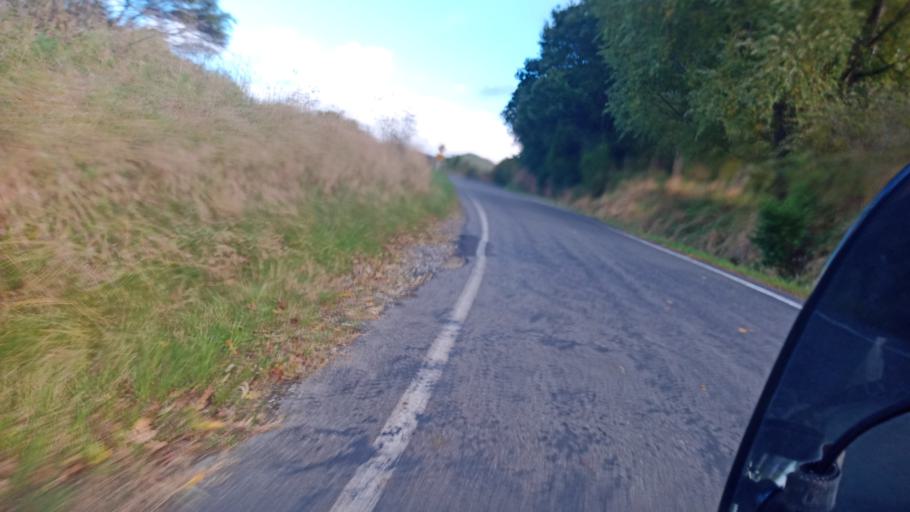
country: NZ
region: Gisborne
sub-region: Gisborne District
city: Gisborne
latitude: -38.5344
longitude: 177.5572
